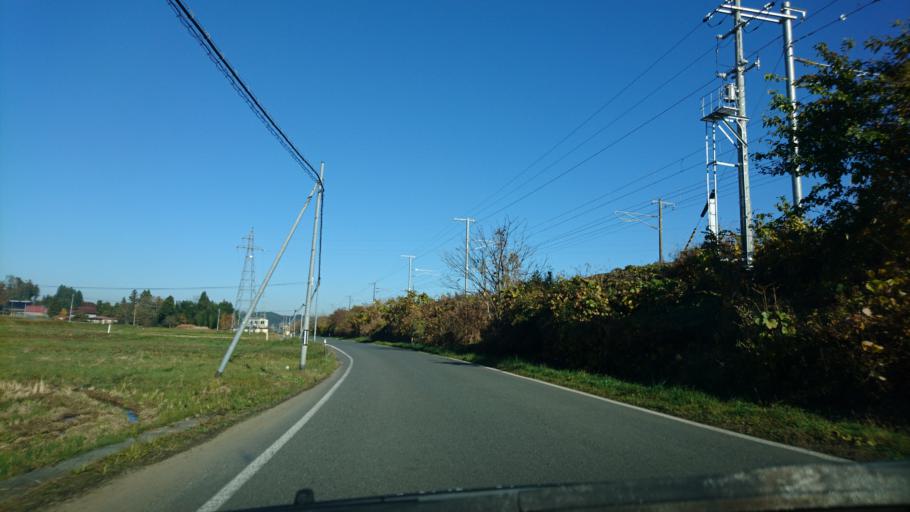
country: JP
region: Iwate
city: Mizusawa
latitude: 39.0259
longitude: 141.1293
